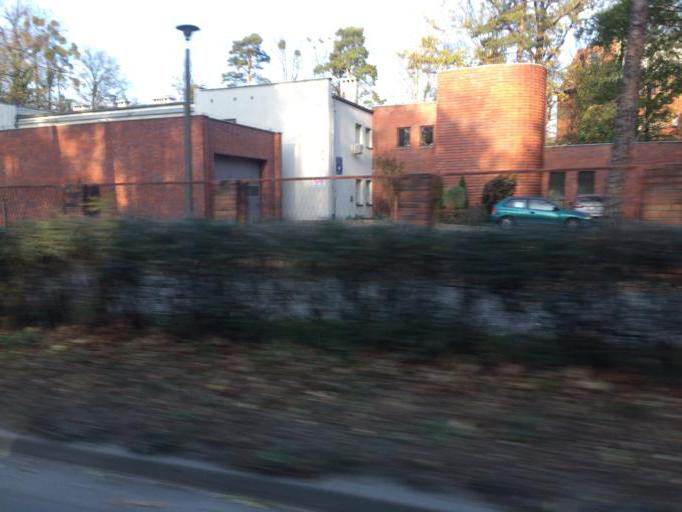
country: PL
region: Opole Voivodeship
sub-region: Powiat strzelecki
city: Strzelce Opolskie
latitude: 50.5146
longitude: 18.2904
